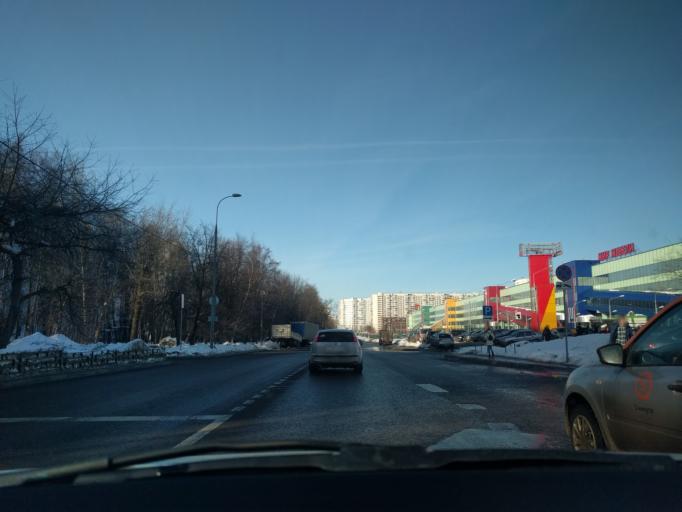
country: RU
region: Moscow
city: Gol'yanovo
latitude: 55.8084
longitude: 37.8296
